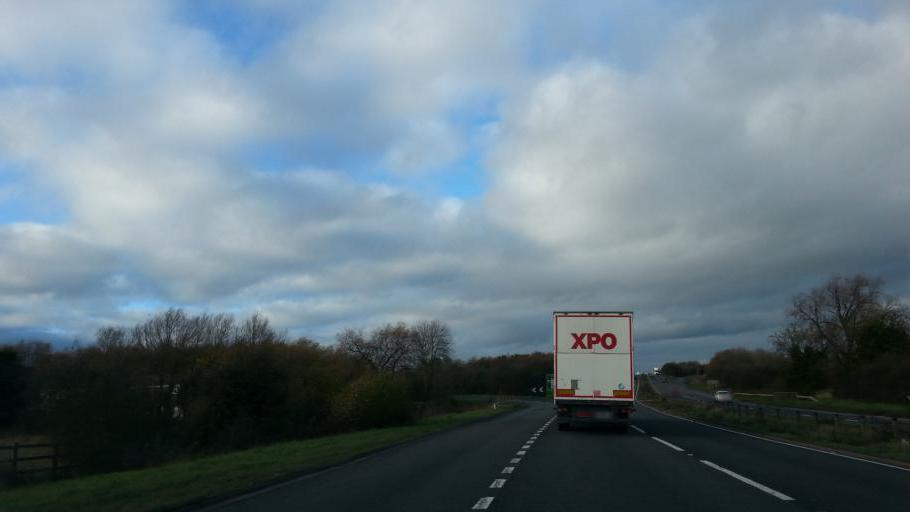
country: GB
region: England
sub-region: Borough of Swindon
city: Wanborough
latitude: 51.5709
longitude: -1.7287
